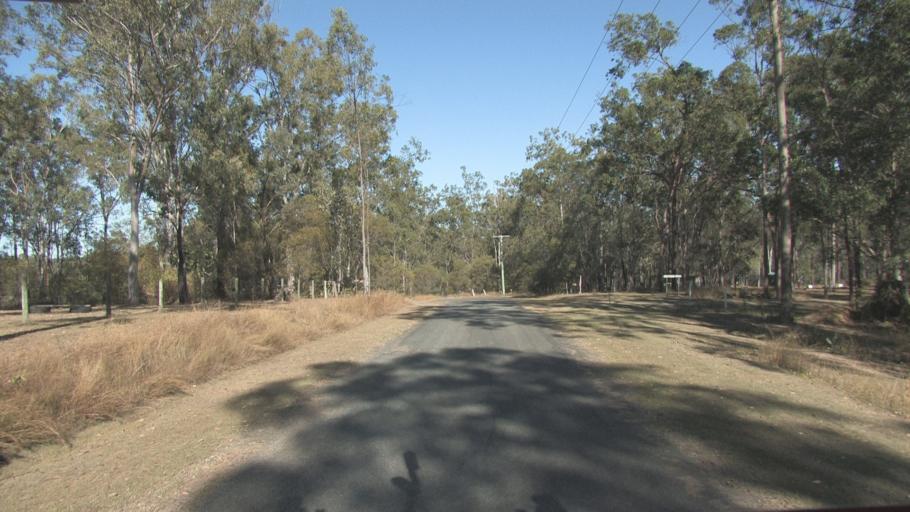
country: AU
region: Queensland
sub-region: Logan
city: Cedar Vale
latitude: -27.8470
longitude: 153.0576
